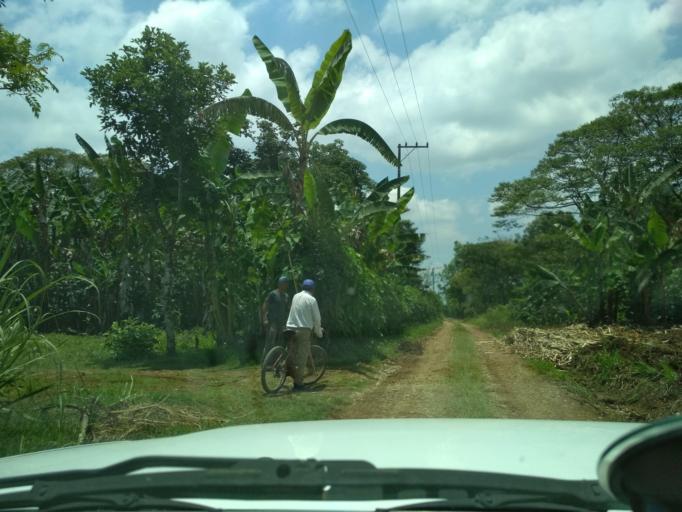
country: MX
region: Veracruz
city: Tocuila
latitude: 18.9533
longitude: -97.0168
